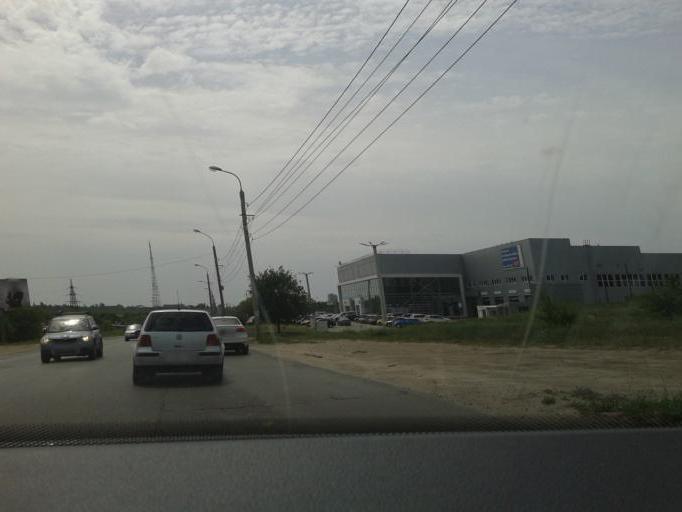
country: RU
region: Volgograd
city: Volgograd
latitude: 48.7578
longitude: 44.5231
